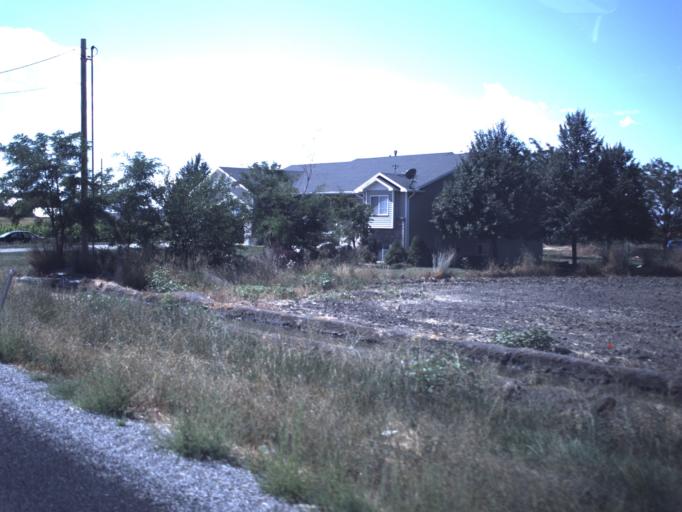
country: US
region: Utah
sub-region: Box Elder County
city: Garland
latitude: 41.7297
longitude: -112.1431
